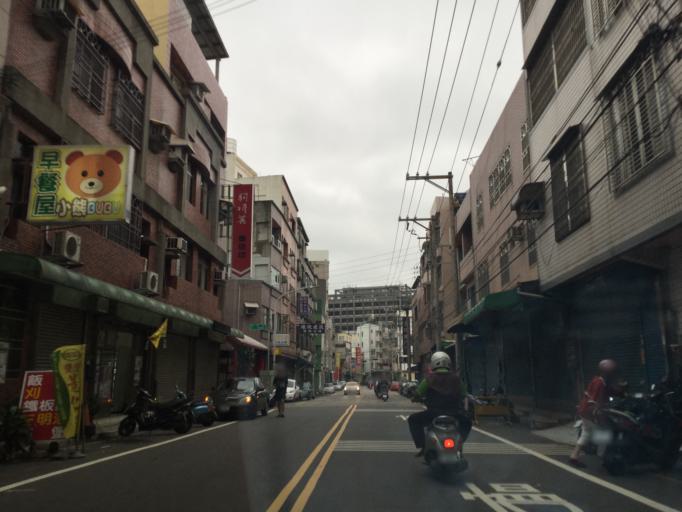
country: TW
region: Taiwan
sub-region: Hsinchu
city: Hsinchu
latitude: 24.7942
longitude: 121.0115
